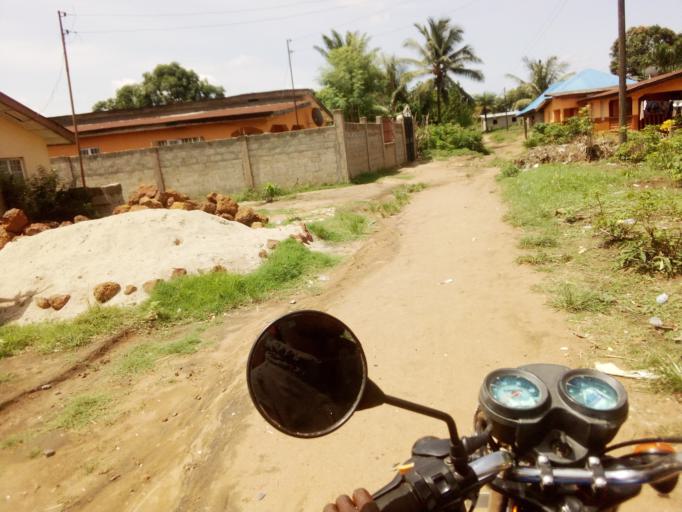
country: SL
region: Western Area
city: Waterloo
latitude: 8.3441
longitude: -13.0703
